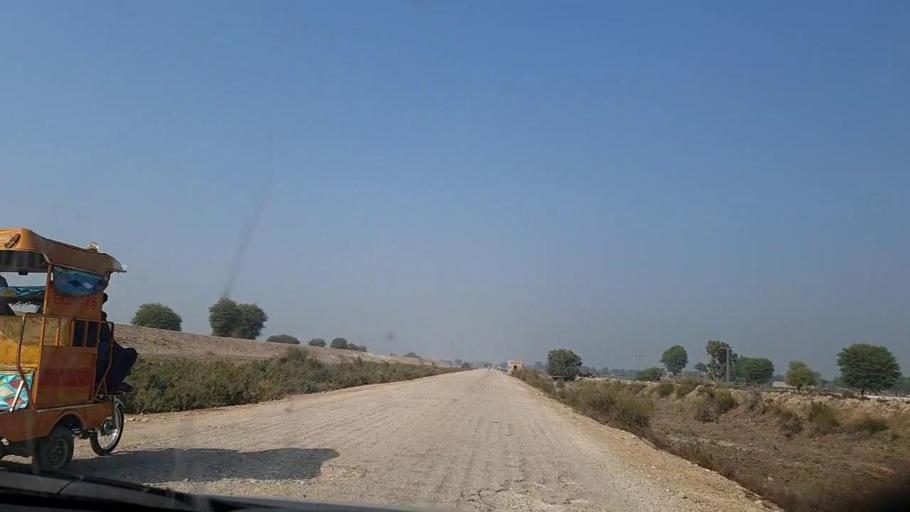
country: PK
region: Sindh
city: Moro
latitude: 26.7223
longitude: 67.9225
